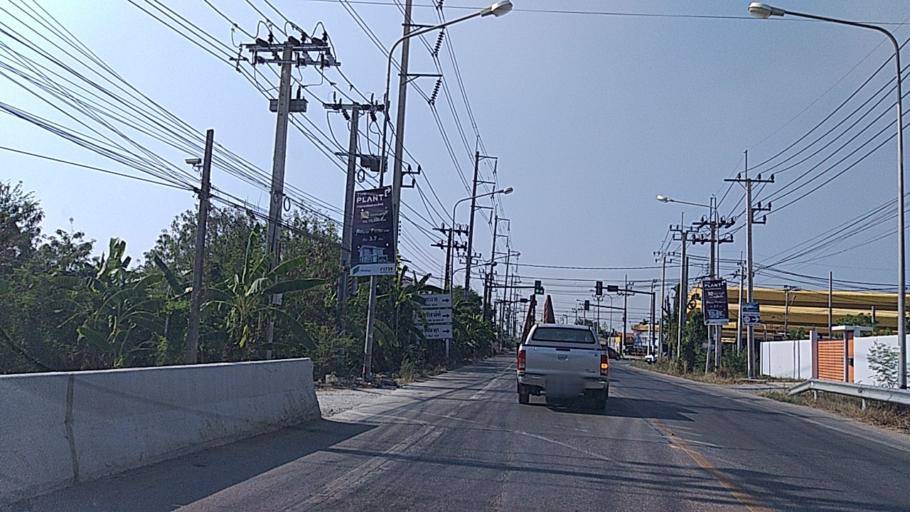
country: TH
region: Nonthaburi
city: Sai Noi
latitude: 13.9085
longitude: 100.3236
